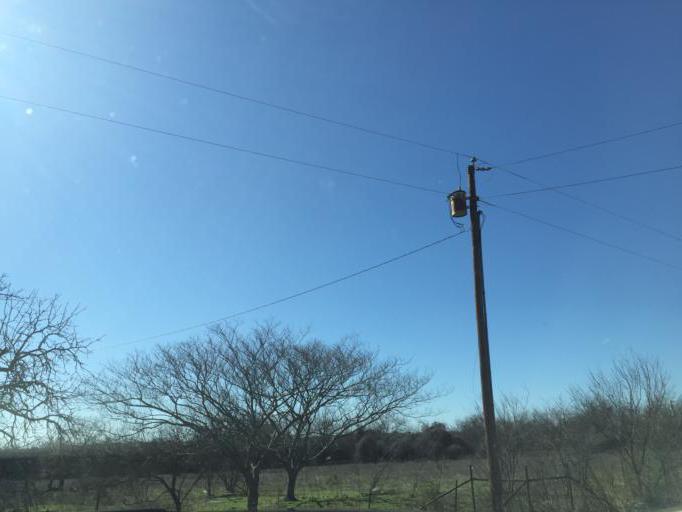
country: US
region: Texas
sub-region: Parker County
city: Weatherford
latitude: 32.7457
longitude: -97.7523
